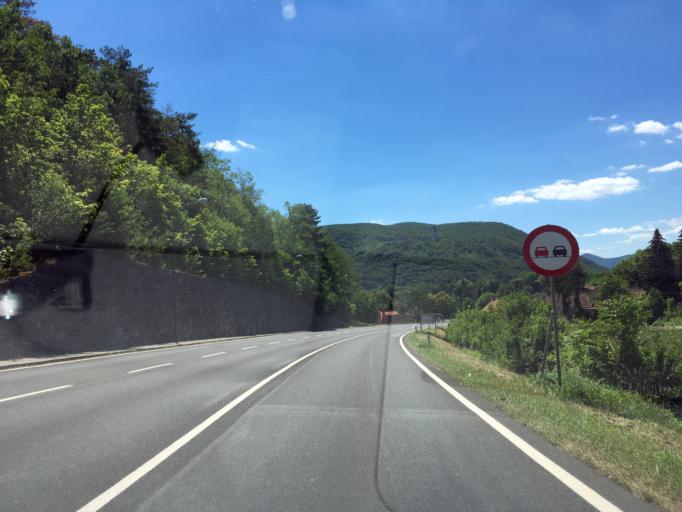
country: AT
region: Lower Austria
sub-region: Politischer Bezirk Neunkirchen
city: Seebenstein
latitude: 47.7066
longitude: 16.1434
